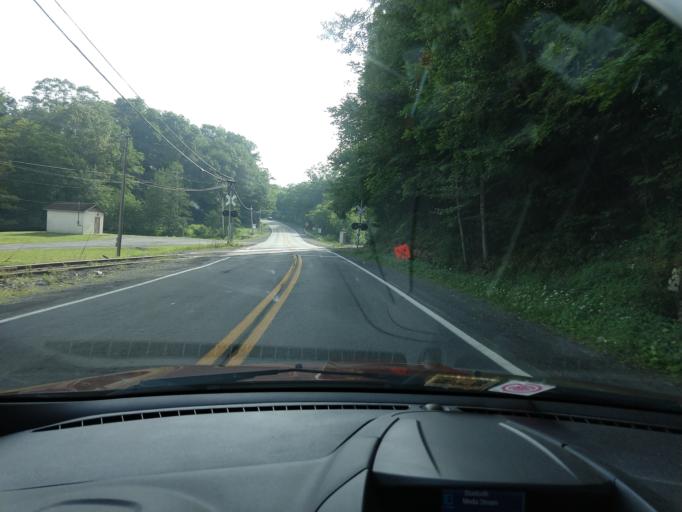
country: US
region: West Virginia
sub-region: Greenbrier County
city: Rainelle
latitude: 38.0538
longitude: -80.7145
